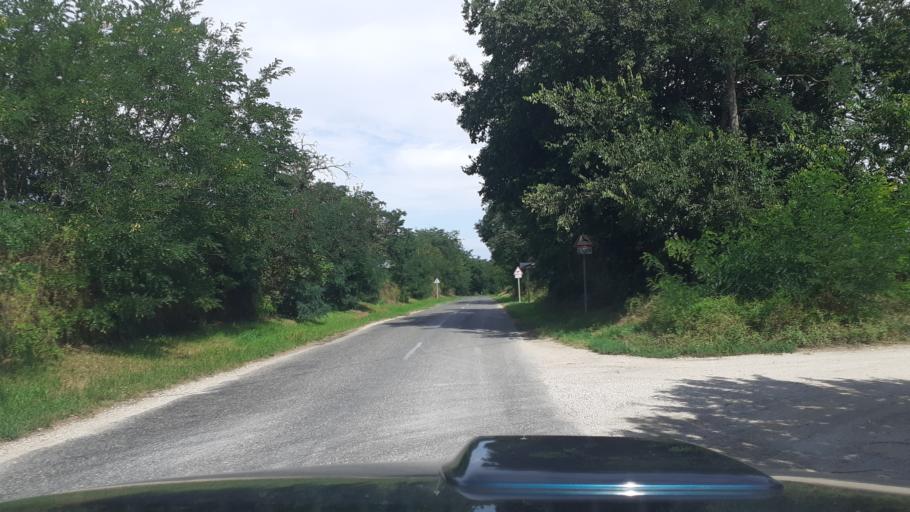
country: HU
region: Fejer
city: Seregelyes
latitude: 47.1244
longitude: 18.5772
